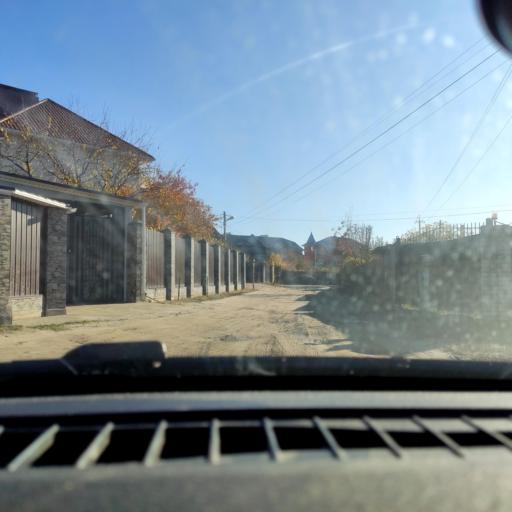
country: RU
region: Voronezj
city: Podgornoye
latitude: 51.7250
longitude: 39.1468
